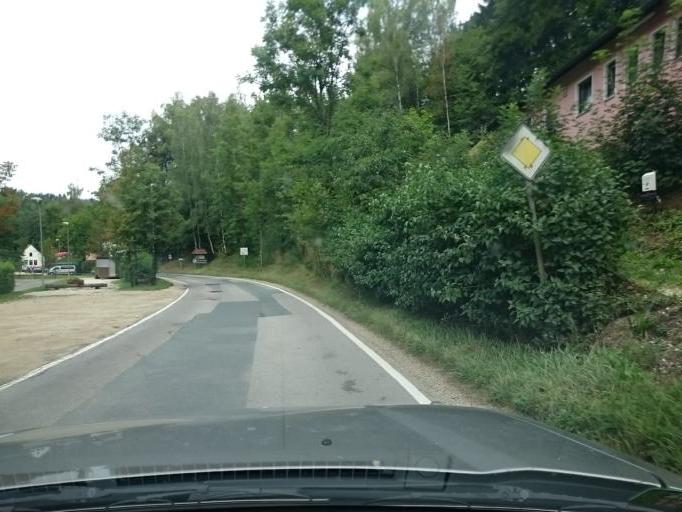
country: DE
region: Bavaria
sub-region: Regierungsbezirk Mittelfranken
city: Velden
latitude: 49.6102
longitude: 11.5091
